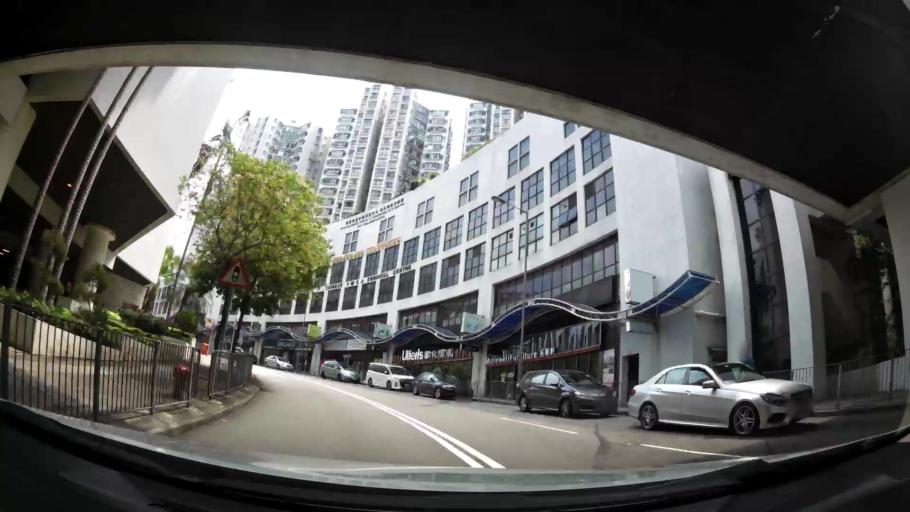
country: HK
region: Wanchai
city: Wan Chai
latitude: 22.2835
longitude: 114.2162
